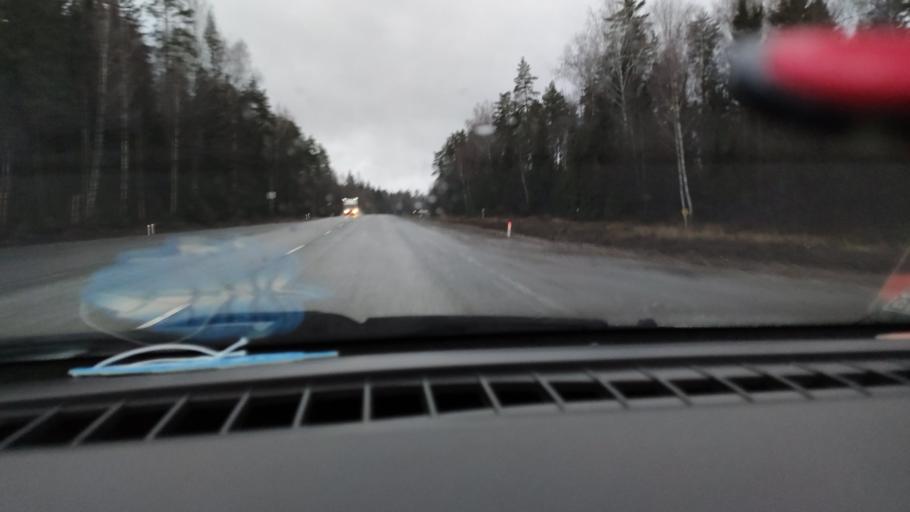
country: RU
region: Udmurtiya
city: Alnashi
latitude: 56.0928
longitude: 52.4477
